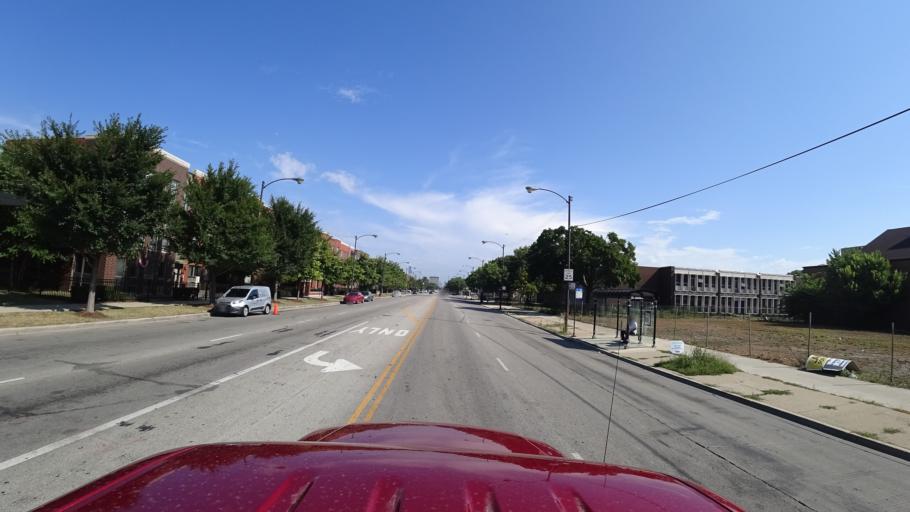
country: US
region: Illinois
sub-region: Cook County
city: Chicago
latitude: 41.8132
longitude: -87.6262
